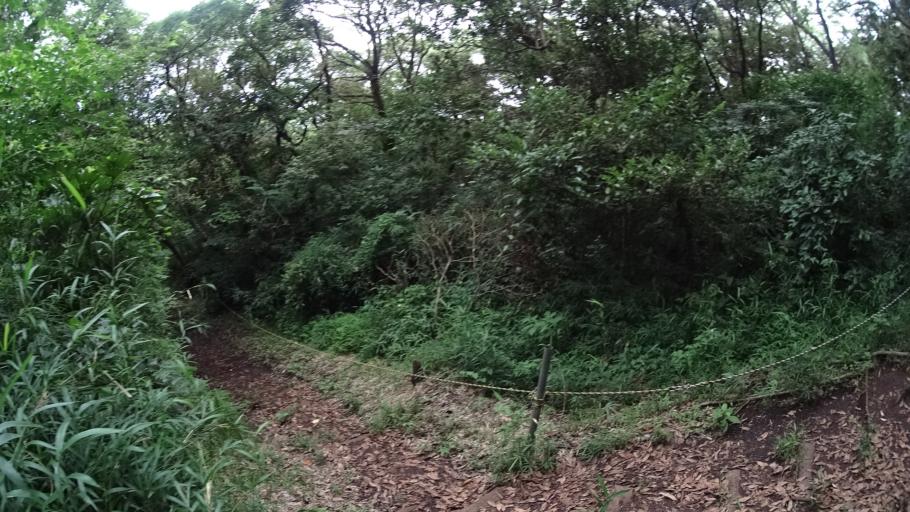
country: JP
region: Kanagawa
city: Yokosuka
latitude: 35.2155
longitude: 139.6560
